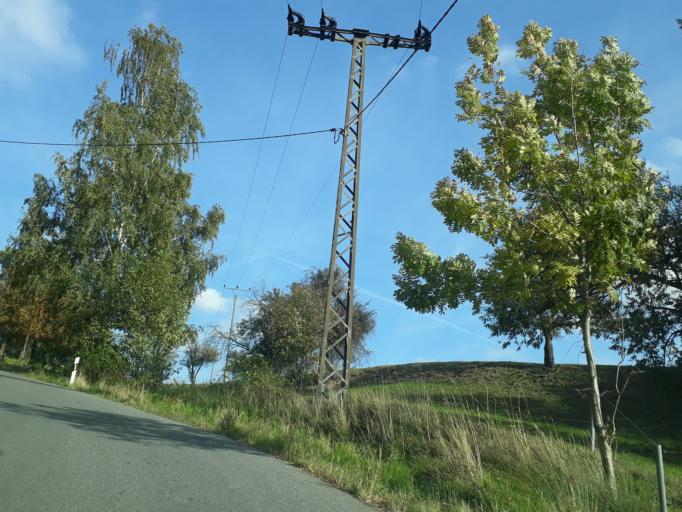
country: DE
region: Saxony
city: Klipphausen
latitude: 51.0852
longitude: 13.5697
